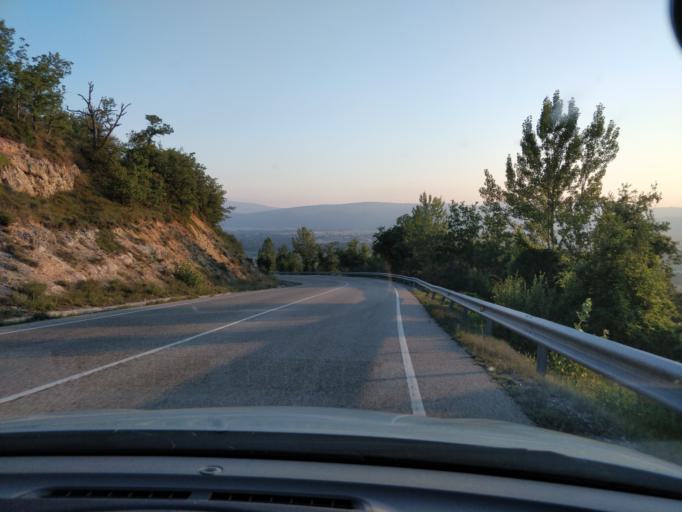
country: ES
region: Castille and Leon
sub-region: Provincia de Burgos
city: Medina de Pomar
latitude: 42.9854
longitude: -3.5342
